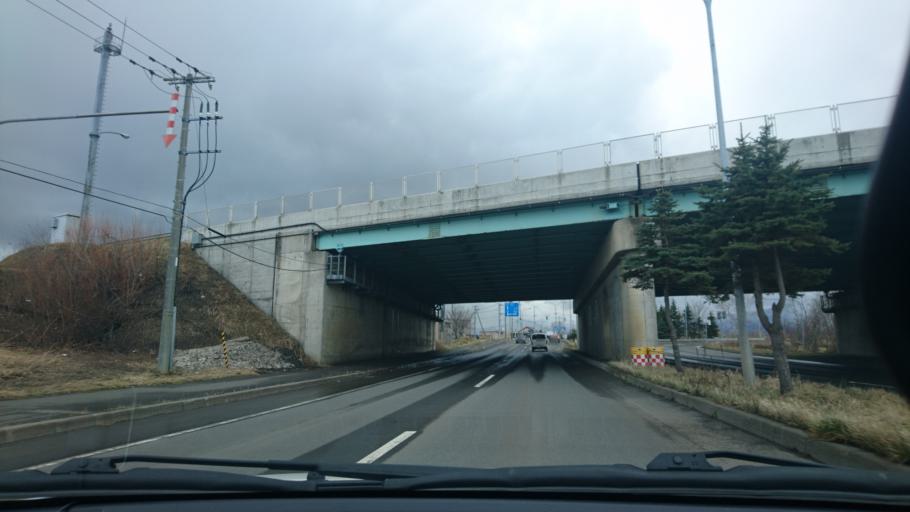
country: JP
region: Hokkaido
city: Ishikari
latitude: 43.1838
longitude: 141.3234
